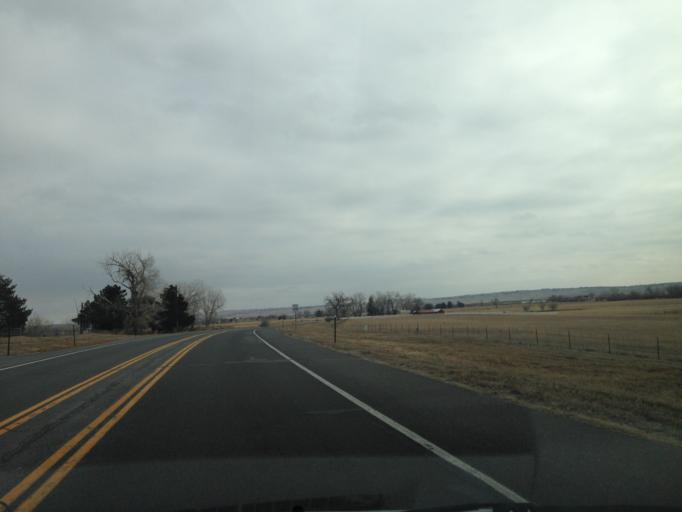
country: US
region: Colorado
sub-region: Boulder County
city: Louisville
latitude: 39.9577
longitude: -105.1440
